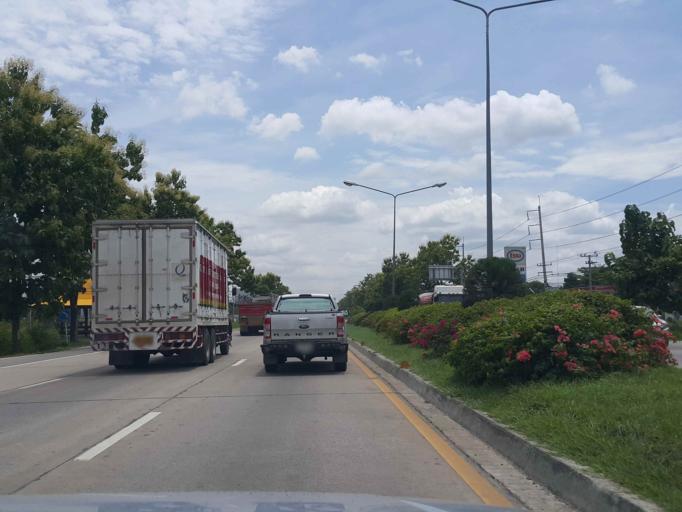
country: TH
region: Lamphun
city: Ban Thi
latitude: 18.6335
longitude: 99.0508
